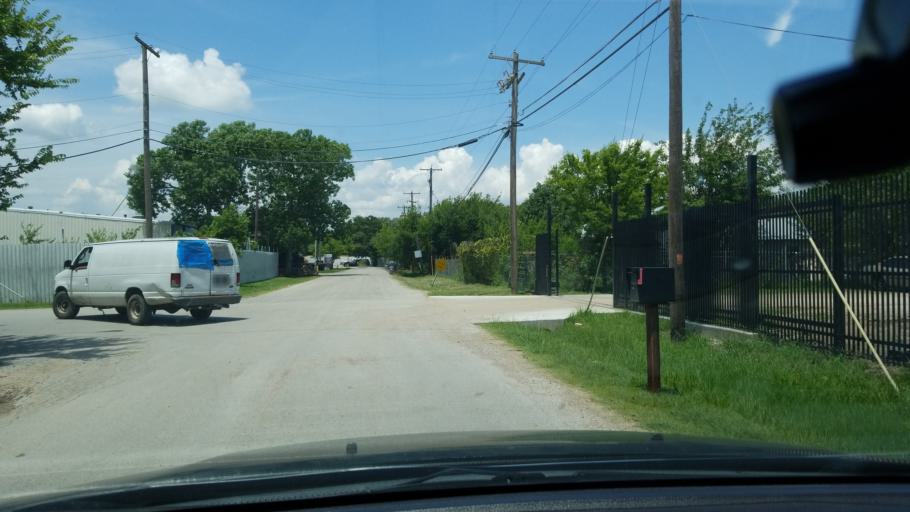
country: US
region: Texas
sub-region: Dallas County
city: Balch Springs
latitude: 32.7414
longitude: -96.6339
